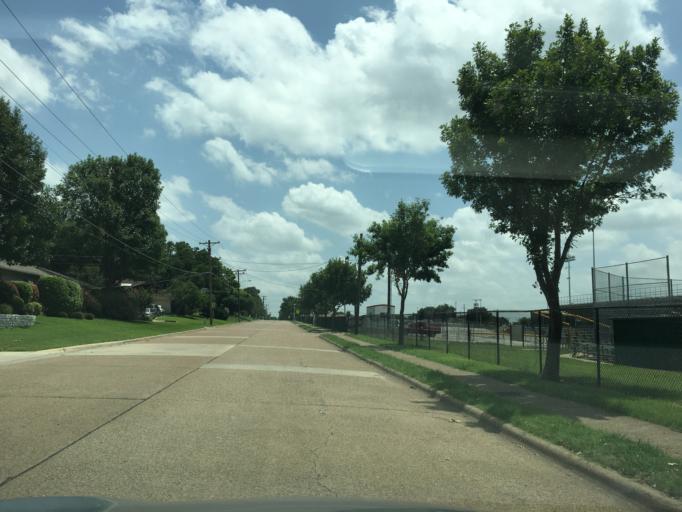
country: US
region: Texas
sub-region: Dallas County
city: University Park
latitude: 32.8864
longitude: -96.7828
